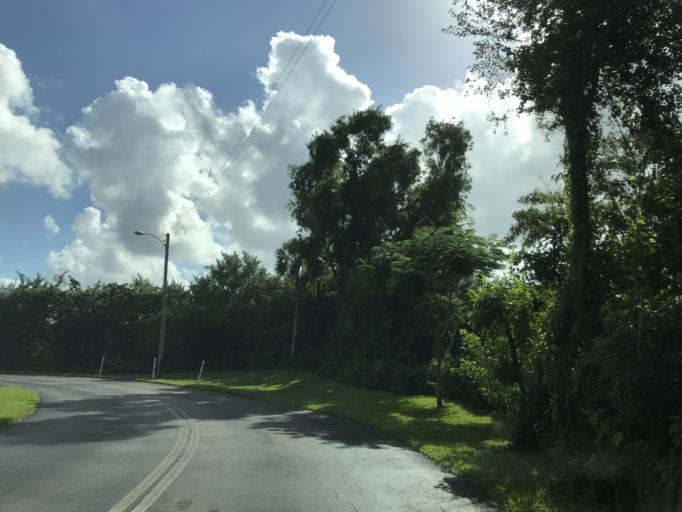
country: US
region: Florida
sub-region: Broward County
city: Margate
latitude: 26.2604
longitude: -80.1976
